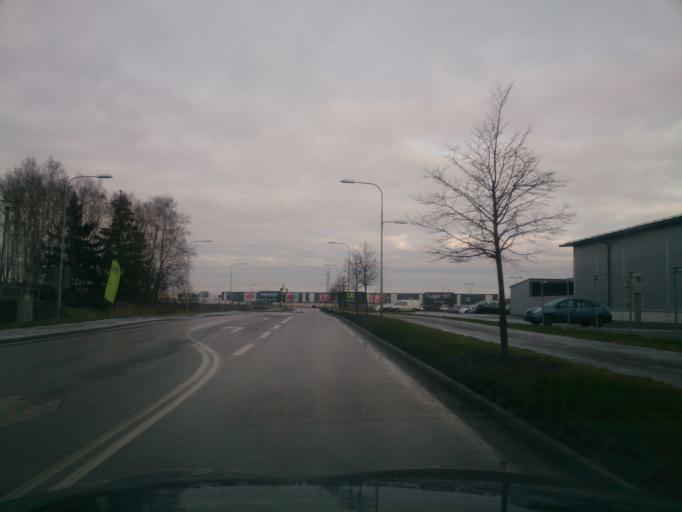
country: SE
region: OEstergoetland
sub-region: Linkopings Kommun
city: Linkoping
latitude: 58.4304
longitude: 15.6034
